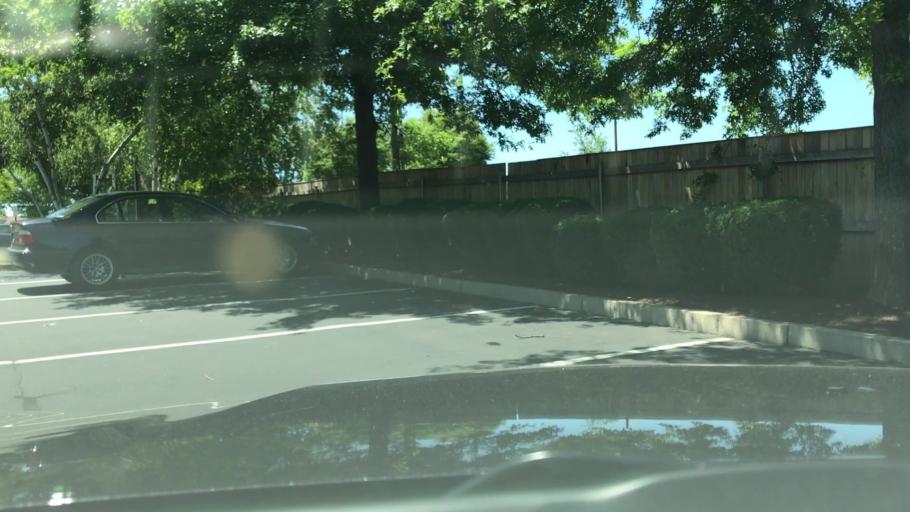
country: US
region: Rhode Island
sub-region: Providence County
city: Cranston
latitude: 41.7547
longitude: -71.4344
